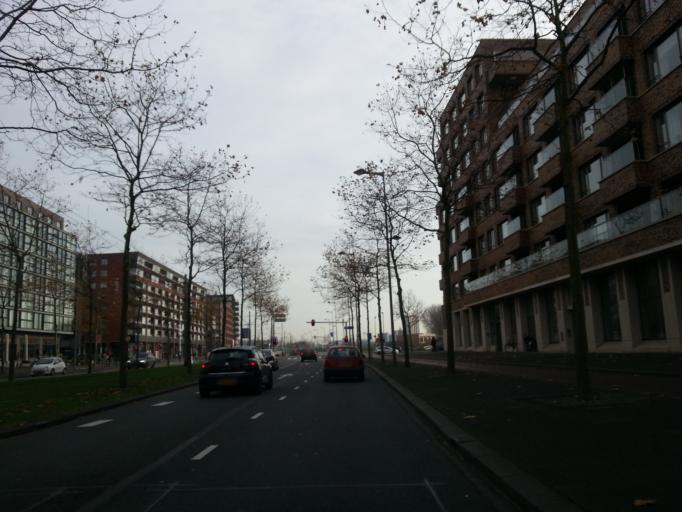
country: NL
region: South Holland
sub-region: Gemeente Rotterdam
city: Rotterdam
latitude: 51.9048
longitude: 4.5012
